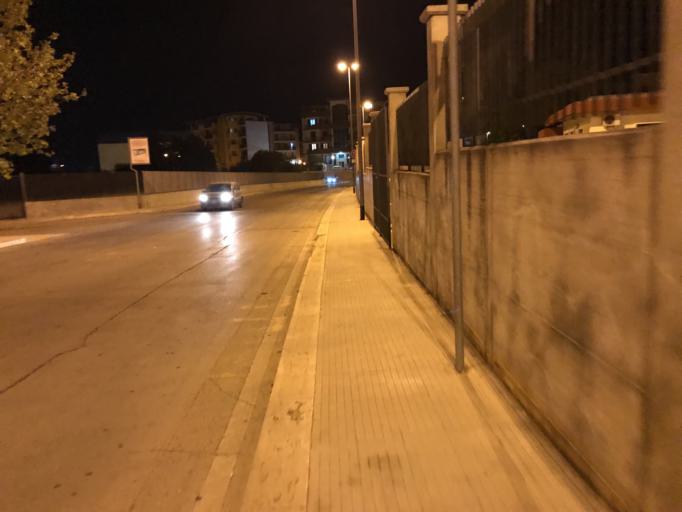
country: IT
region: Apulia
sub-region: Provincia di Bari
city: Corato
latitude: 41.1523
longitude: 16.4017
